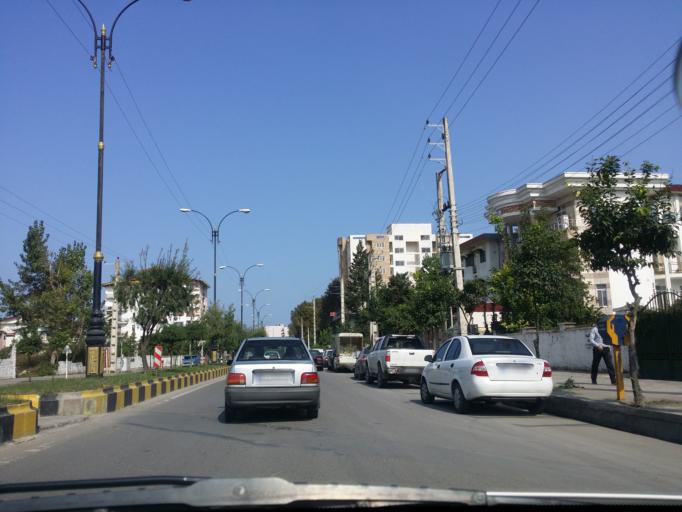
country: IR
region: Mazandaran
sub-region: Nowshahr
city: Nowshahr
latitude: 36.6391
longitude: 51.4896
